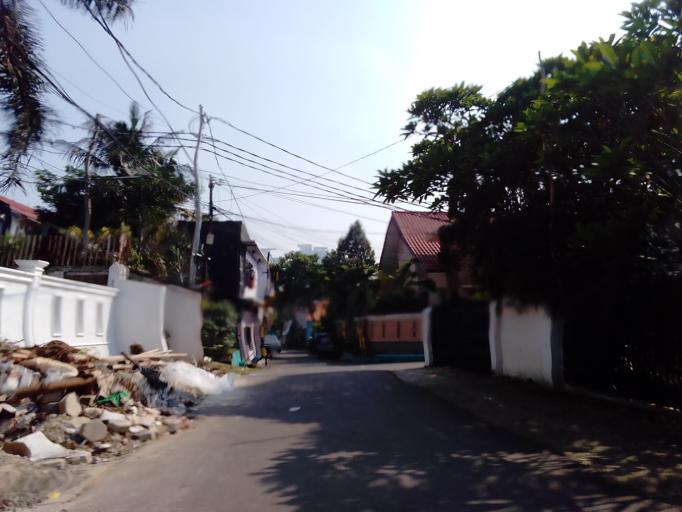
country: ID
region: Jakarta Raya
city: Jakarta
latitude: -6.2657
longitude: 106.8052
